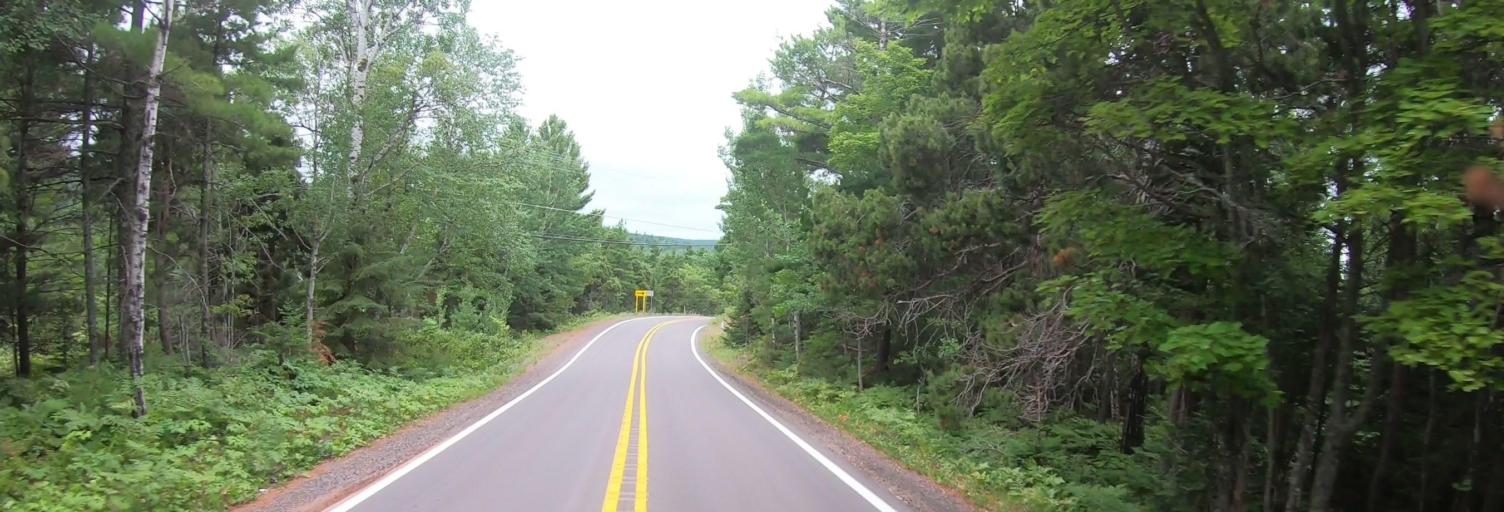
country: US
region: Michigan
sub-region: Keweenaw County
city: Eagle River
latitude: 47.4594
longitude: -88.1227
